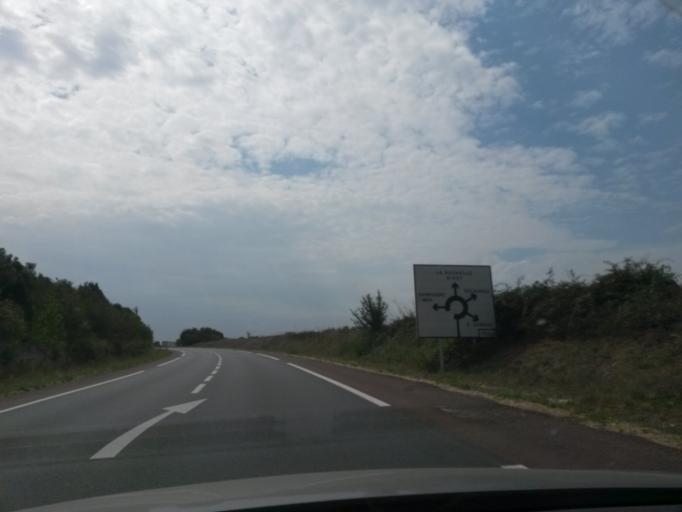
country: FR
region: Poitou-Charentes
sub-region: Departement de la Charente-Maritime
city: Saint-Xandre
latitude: 46.1979
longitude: -1.0953
